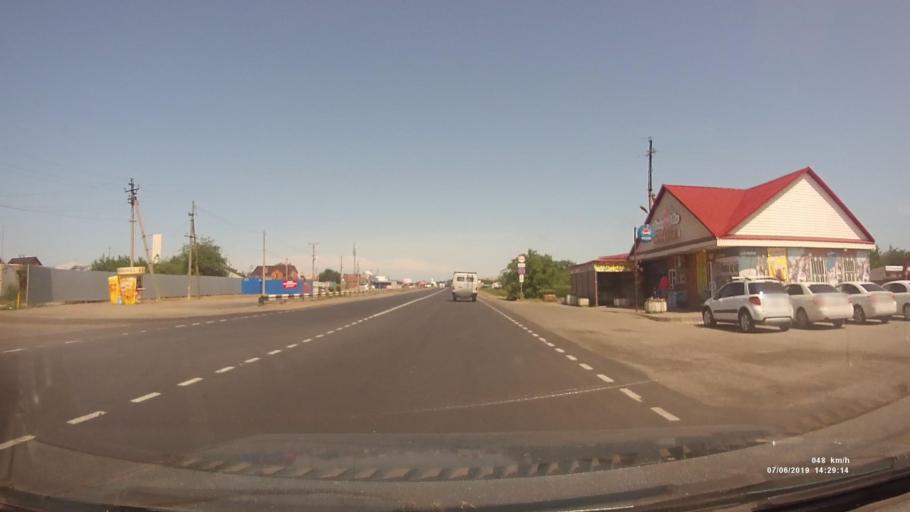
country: RU
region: Rostov
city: Kuleshovka
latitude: 47.0800
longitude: 39.5756
